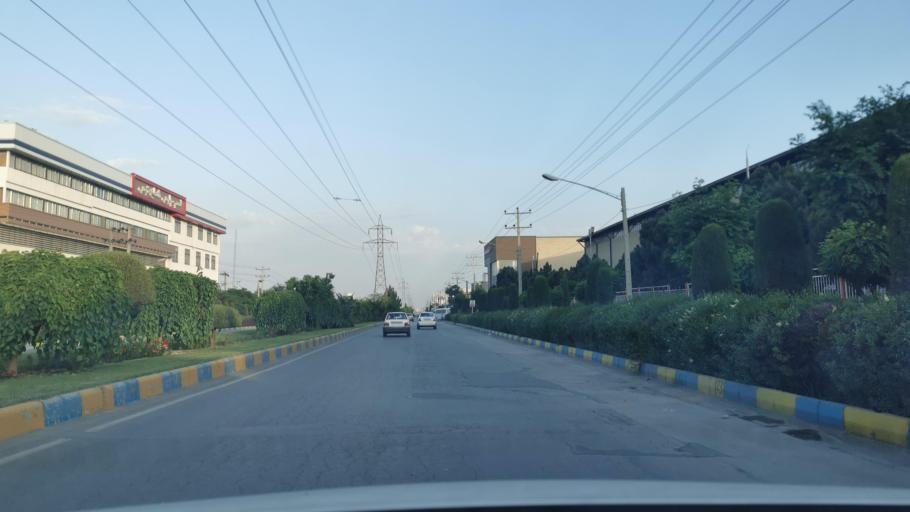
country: IR
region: Razavi Khorasan
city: Torqabeh
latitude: 36.4274
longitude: 59.4210
